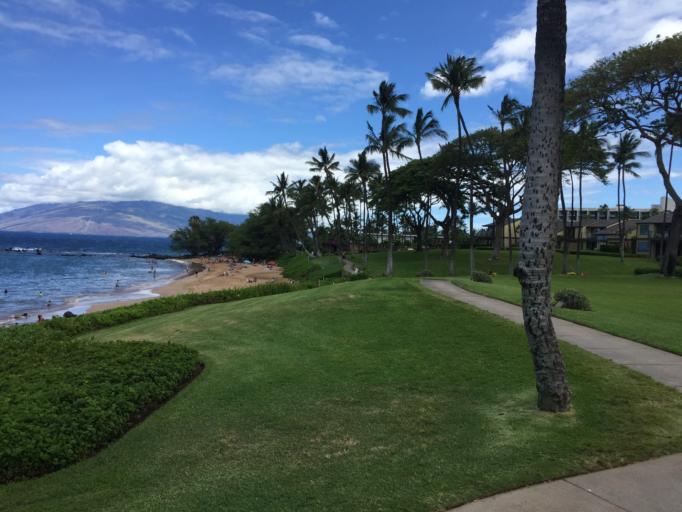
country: US
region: Hawaii
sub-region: Maui County
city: Kihei
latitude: 20.6898
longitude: -156.4433
